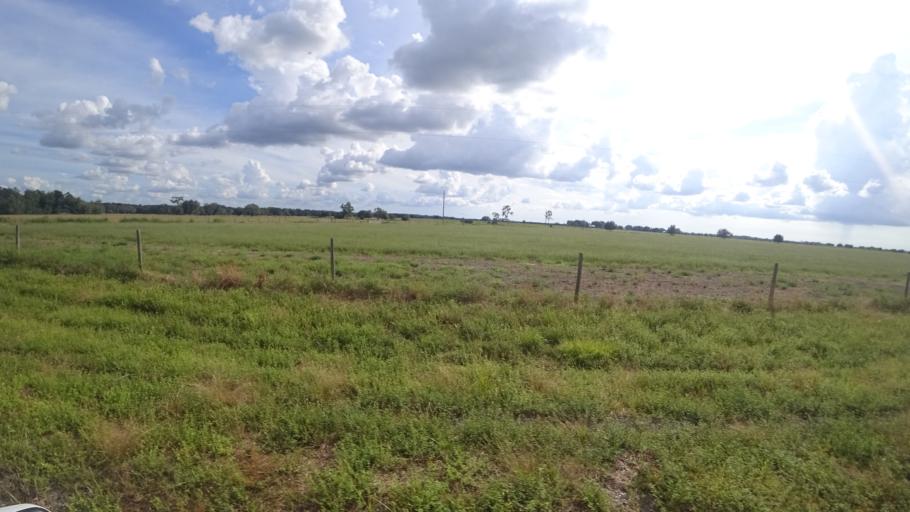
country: US
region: Florida
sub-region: Sarasota County
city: Lake Sarasota
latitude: 27.3391
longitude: -82.1773
